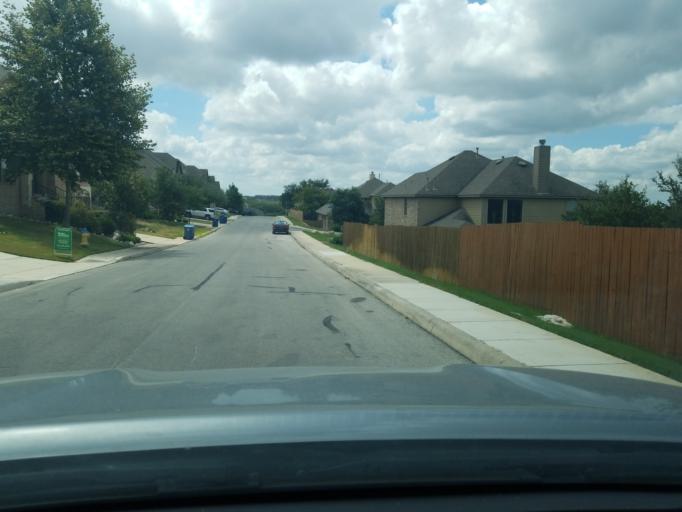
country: US
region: Texas
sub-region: Bexar County
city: Timberwood Park
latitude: 29.6654
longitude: -98.5057
